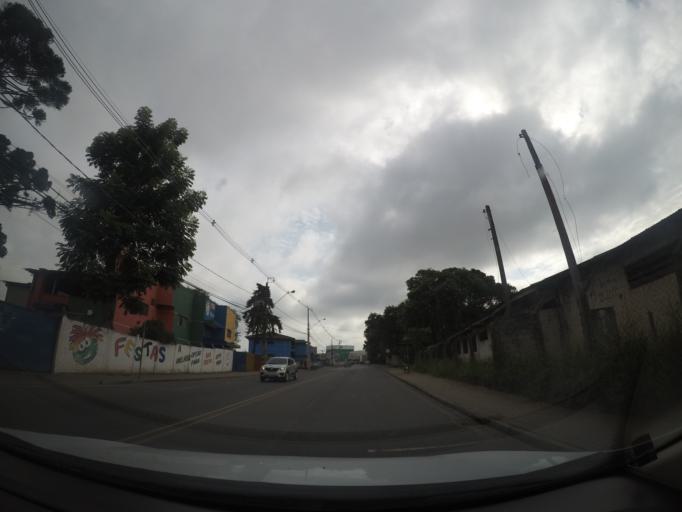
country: BR
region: Parana
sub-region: Colombo
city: Colombo
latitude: -25.3540
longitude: -49.2003
